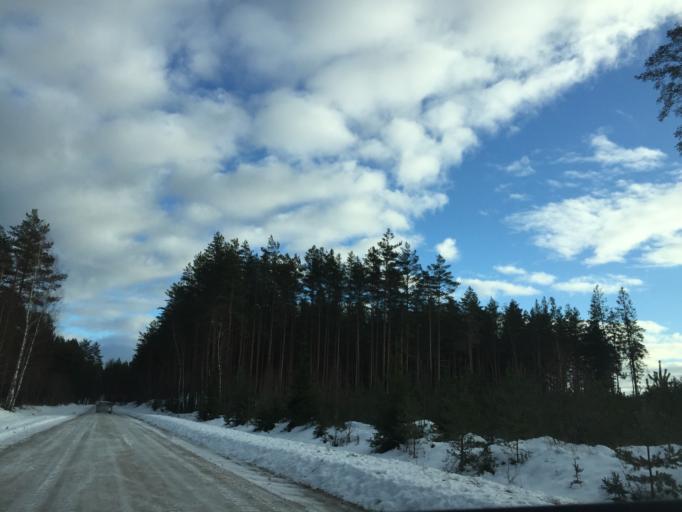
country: LV
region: Lielvarde
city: Lielvarde
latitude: 56.5622
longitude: 24.8380
